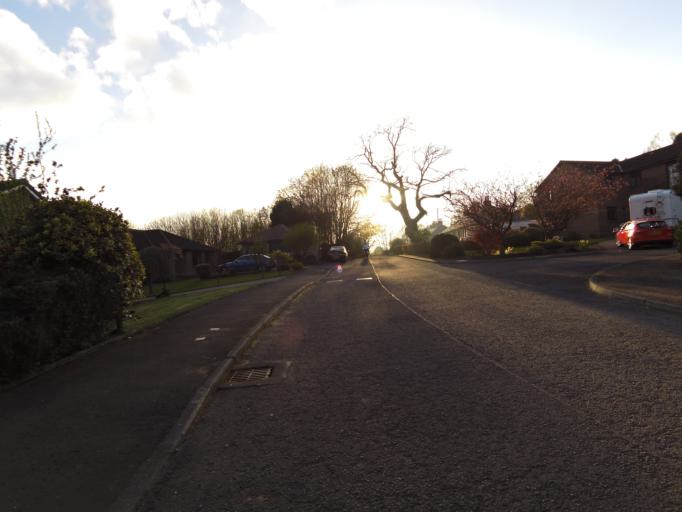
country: GB
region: Scotland
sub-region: Fife
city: Leslie
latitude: 56.2097
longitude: -3.2005
